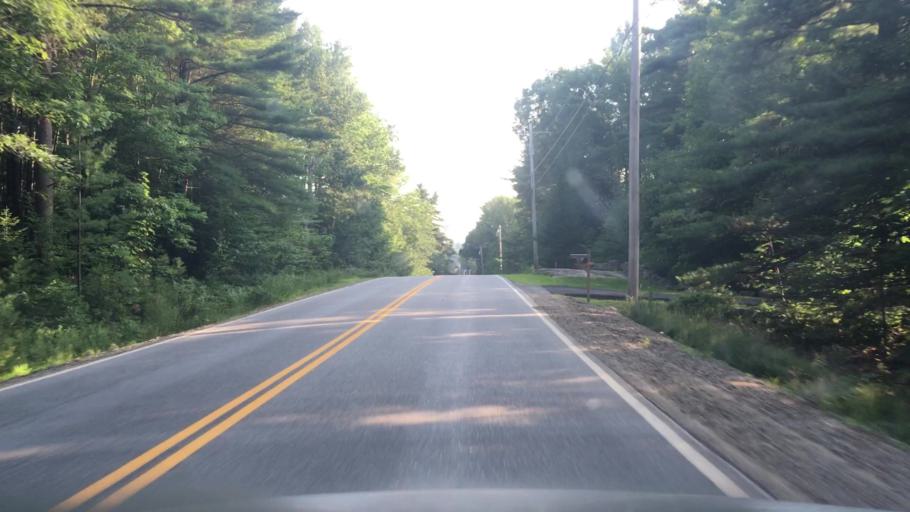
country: US
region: Maine
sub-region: Androscoggin County
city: Lisbon Falls
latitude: 43.9389
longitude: -70.0771
